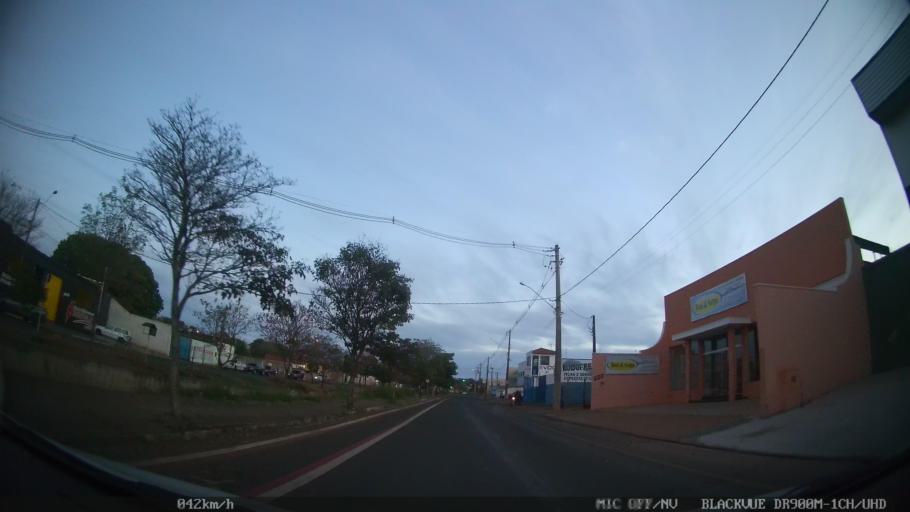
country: BR
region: Sao Paulo
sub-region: Catanduva
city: Catanduva
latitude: -21.1283
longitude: -48.9843
